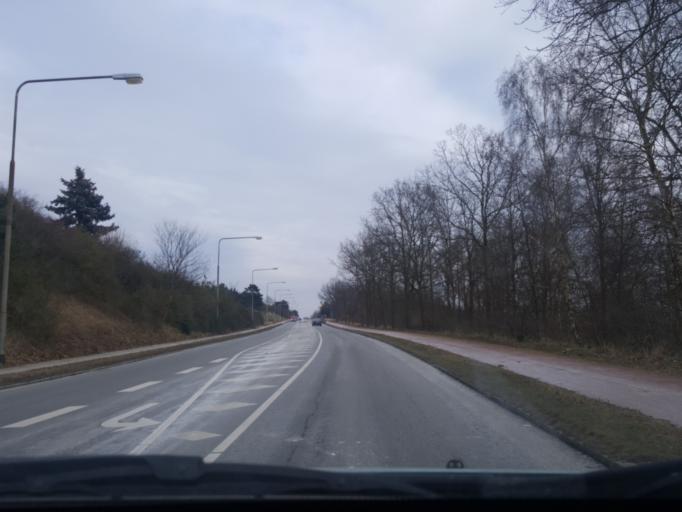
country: DK
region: Zealand
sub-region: Kalundborg Kommune
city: Kalundborg
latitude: 55.6866
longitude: 11.0745
